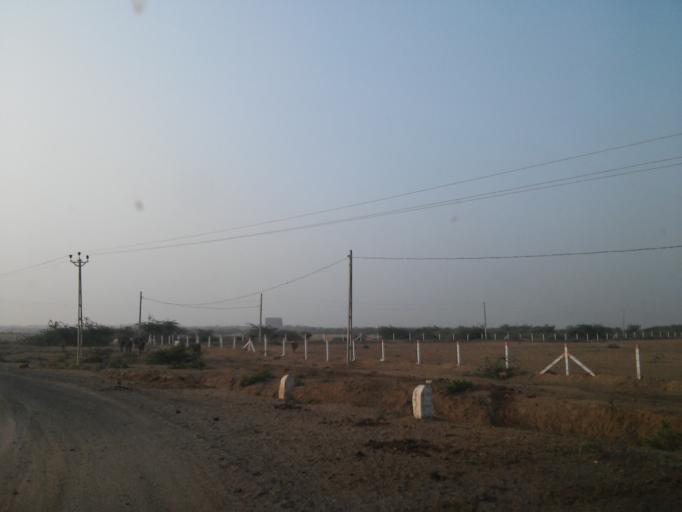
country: IN
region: Gujarat
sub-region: Kachchh
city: Mandvi
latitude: 22.8288
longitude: 69.3862
